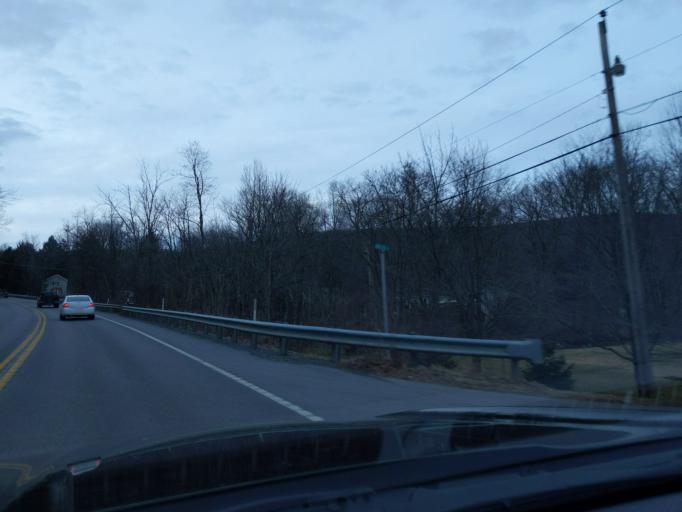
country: US
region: Pennsylvania
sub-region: Blair County
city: Lakemont
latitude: 40.4592
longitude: -78.3577
